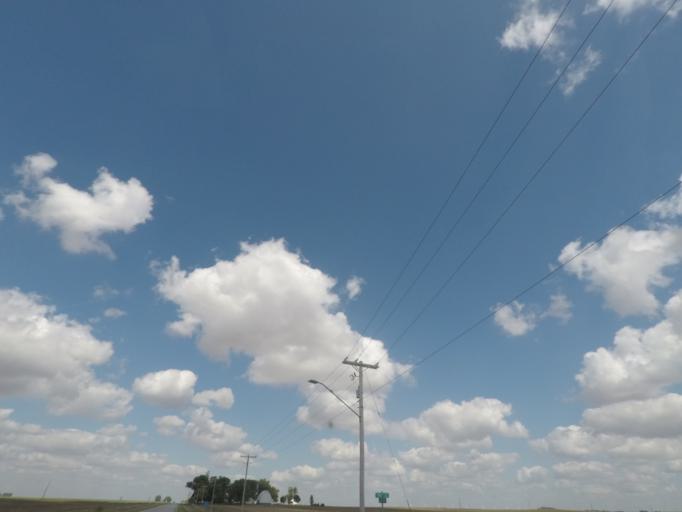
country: US
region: Iowa
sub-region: Story County
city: Nevada
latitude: 42.0778
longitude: -93.3863
